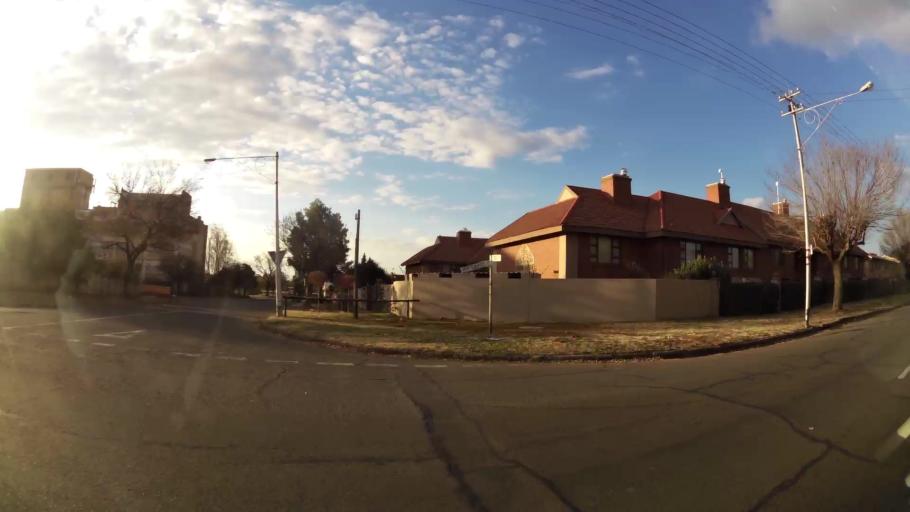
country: ZA
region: Orange Free State
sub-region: Mangaung Metropolitan Municipality
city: Bloemfontein
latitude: -29.1355
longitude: 26.1954
